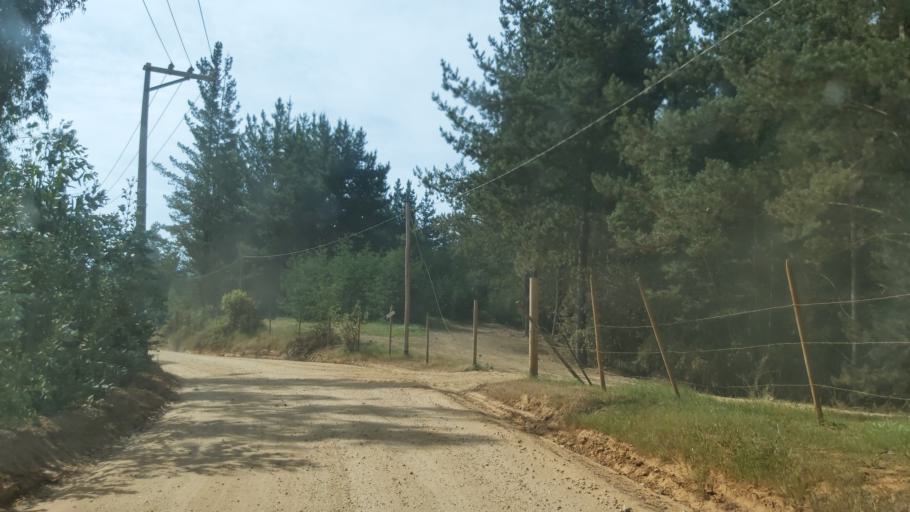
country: CL
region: Maule
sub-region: Provincia de Talca
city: Constitucion
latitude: -34.8481
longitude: -72.0346
